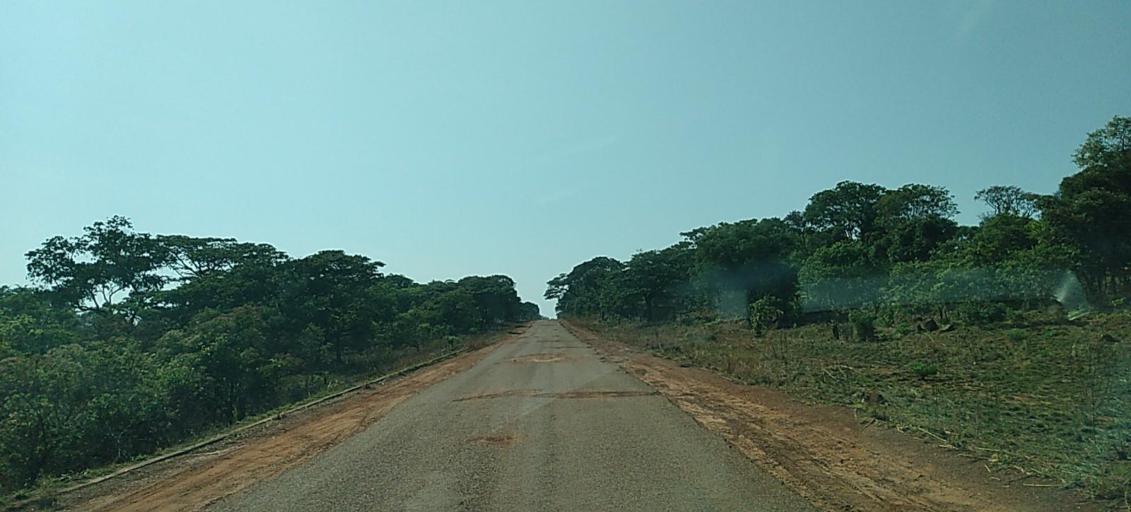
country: ZM
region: North-Western
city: Mwinilunga
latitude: -11.9034
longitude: 25.2838
